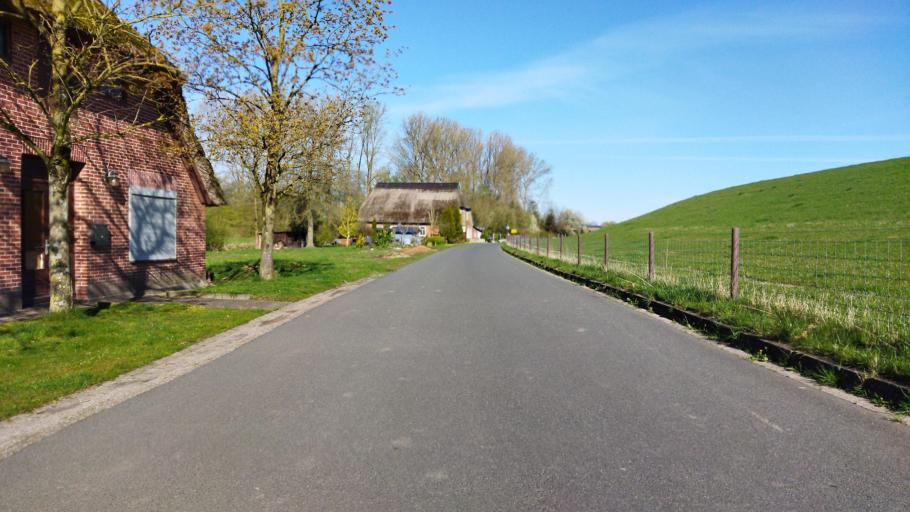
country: DE
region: Lower Saxony
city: Elsfleth
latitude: 53.2063
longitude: 8.4878
